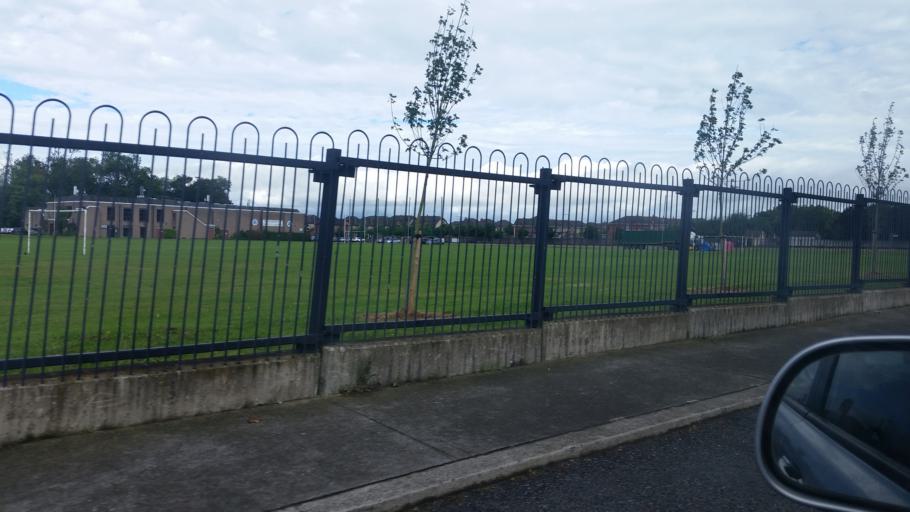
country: IE
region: Leinster
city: Portmarnock
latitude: 53.4335
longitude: -6.1365
